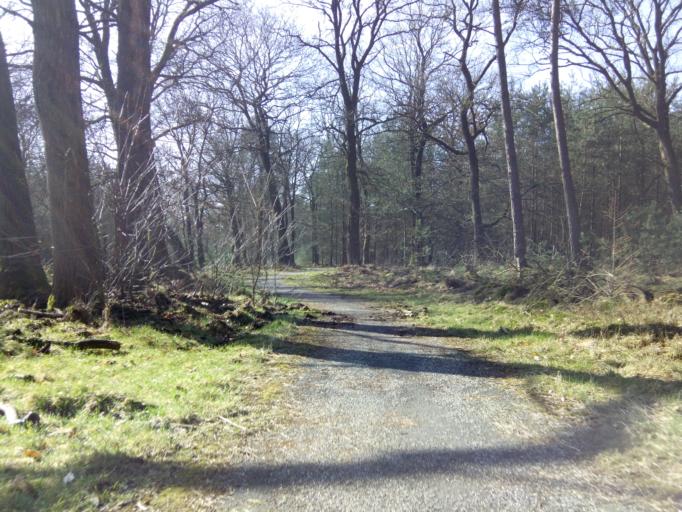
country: NL
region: Gelderland
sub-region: Gemeente Barneveld
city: Garderen
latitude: 52.1901
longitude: 5.7496
